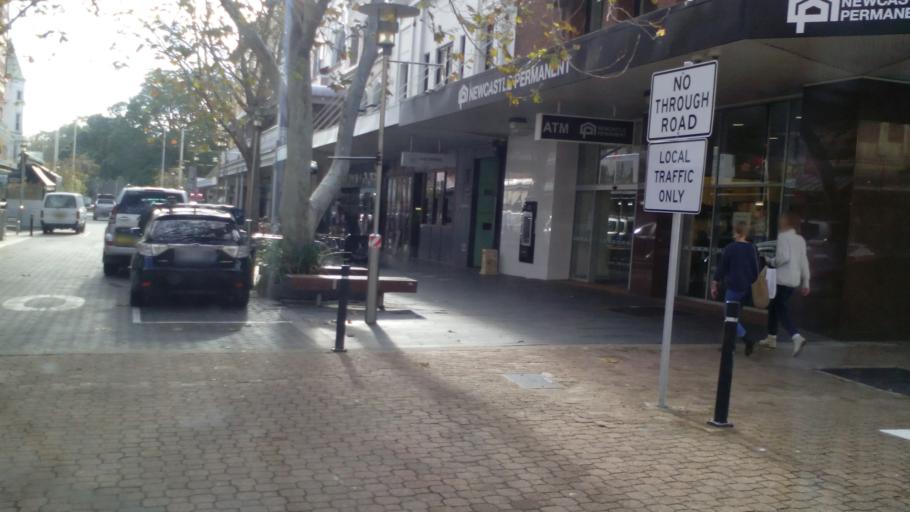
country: AU
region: New South Wales
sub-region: Newcastle
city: Newcastle
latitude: -32.9271
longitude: 151.7805
